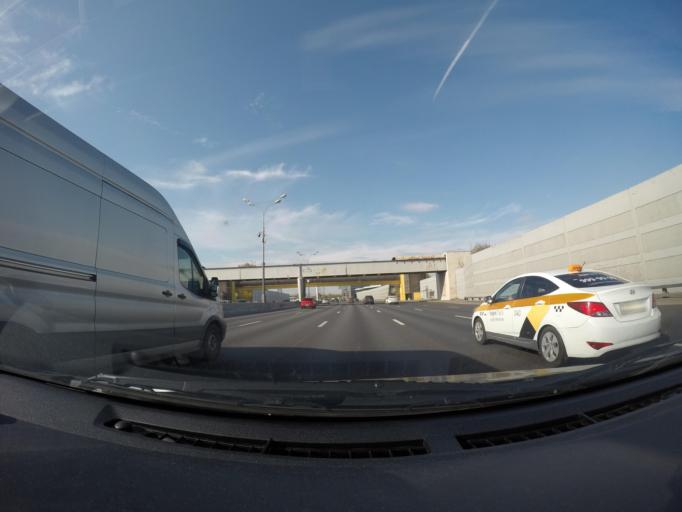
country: RU
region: Moscow
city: Yaroslavskiy
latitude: 55.8927
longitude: 37.7044
